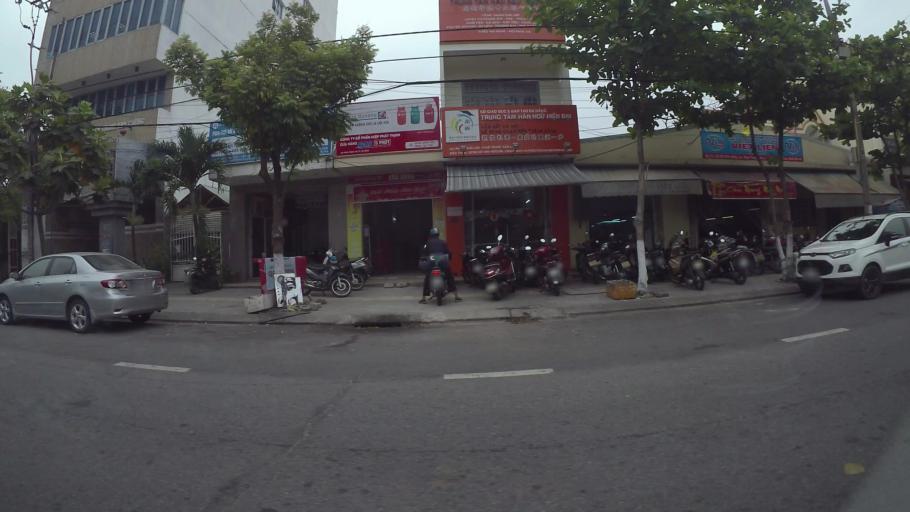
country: VN
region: Da Nang
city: Cam Le
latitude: 16.0366
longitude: 108.2111
